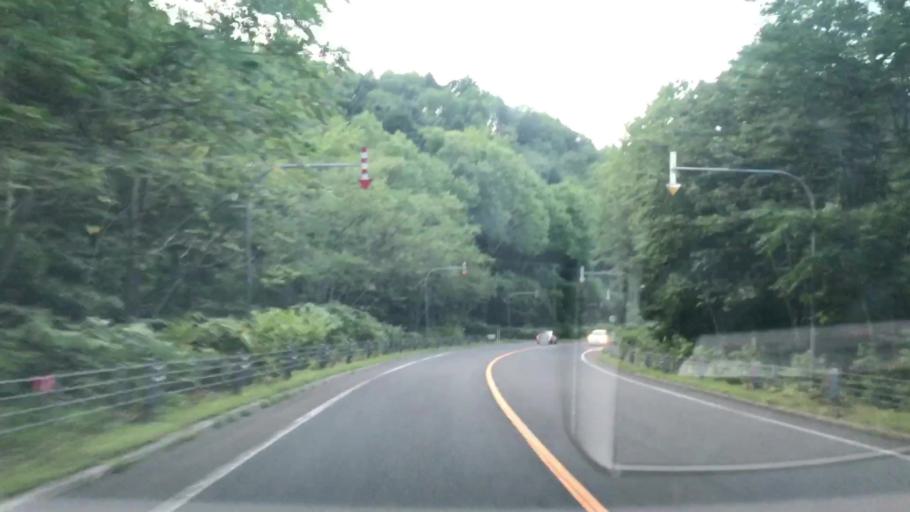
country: JP
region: Hokkaido
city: Sapporo
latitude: 42.9222
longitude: 141.1229
